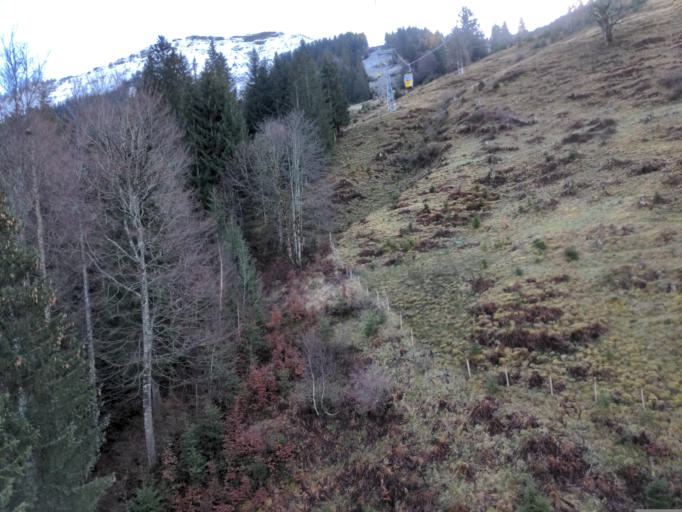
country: DE
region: Bavaria
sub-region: Swabia
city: Balderschwang
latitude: 47.5055
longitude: 10.0614
